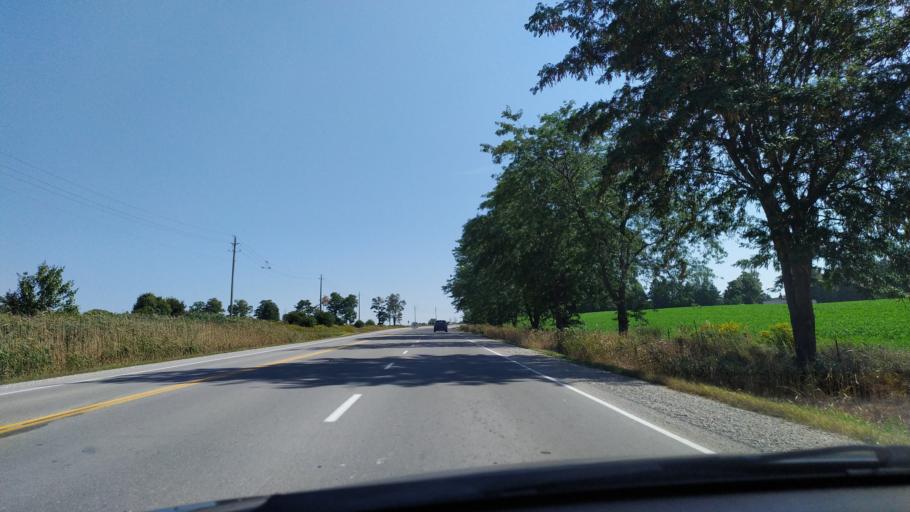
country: CA
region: Ontario
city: Ingersoll
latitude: 43.0662
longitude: -80.8430
